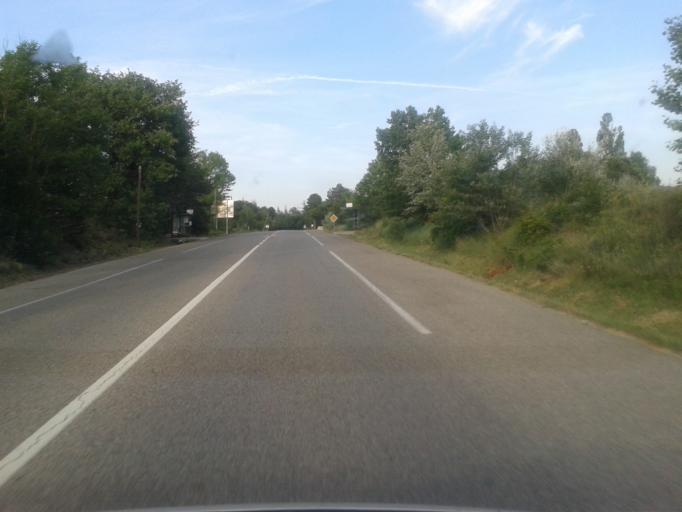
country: FR
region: Provence-Alpes-Cote d'Azur
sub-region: Departement du Vaucluse
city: Beaumont-de-Pertuis
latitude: 43.7006
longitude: 5.7412
